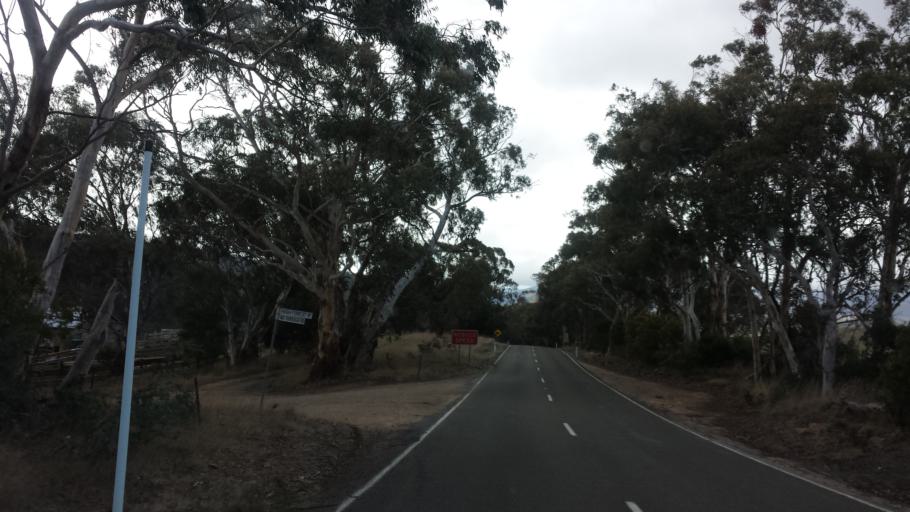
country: AU
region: Victoria
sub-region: Alpine
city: Mount Beauty
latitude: -37.1231
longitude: 147.5404
